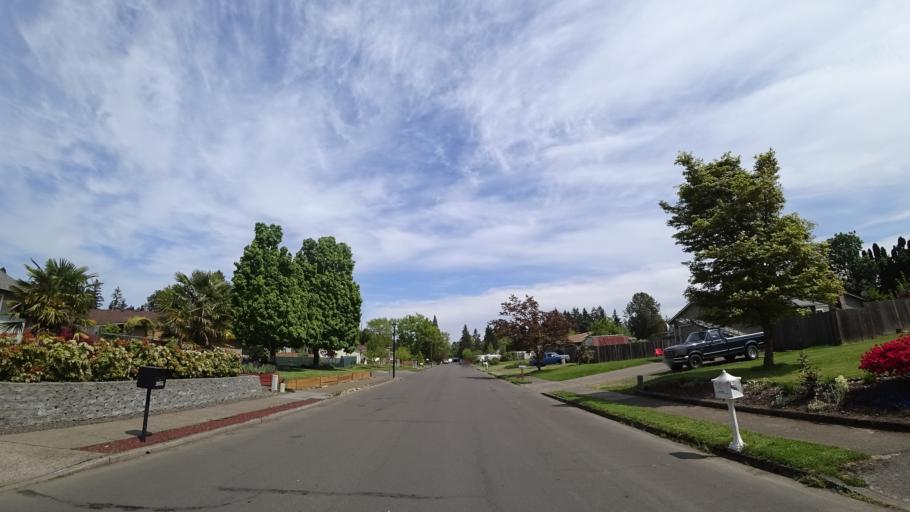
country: US
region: Oregon
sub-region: Washington County
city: Aloha
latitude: 45.4805
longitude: -122.8852
